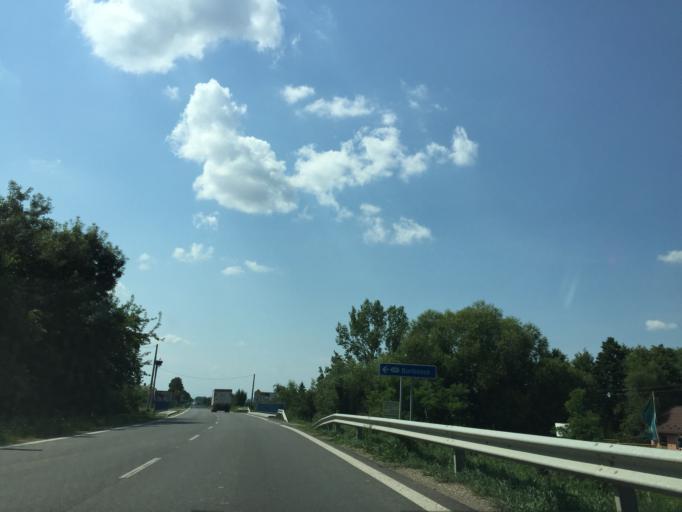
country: SK
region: Kosicky
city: Sobrance
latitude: 48.7550
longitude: 22.1504
